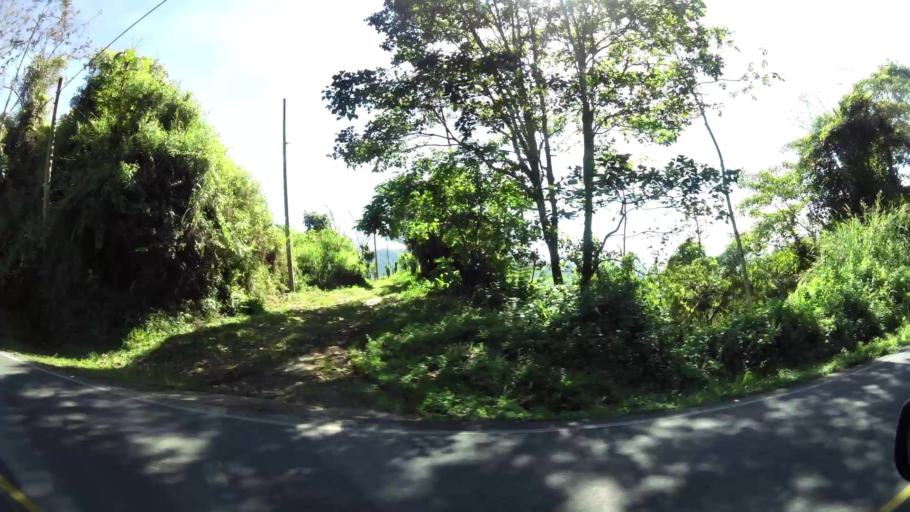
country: CR
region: San Jose
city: San Isidro
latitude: 9.4416
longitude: -83.7123
